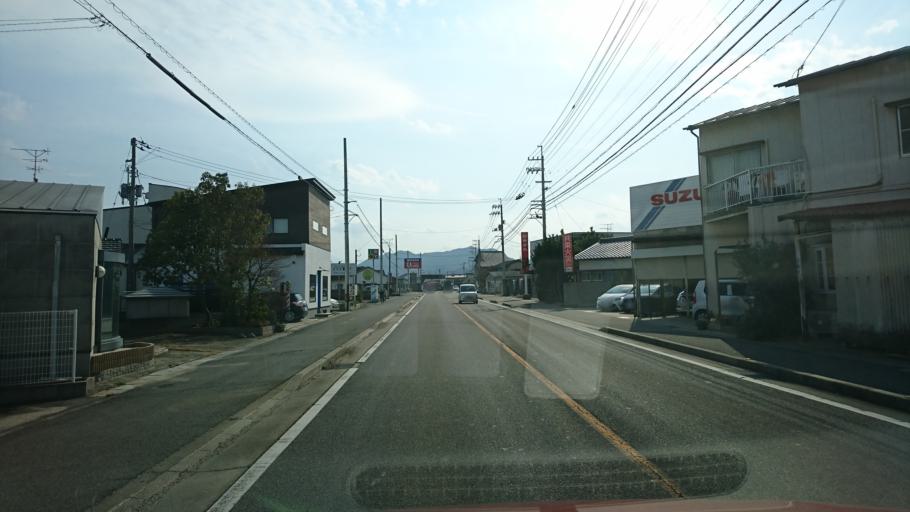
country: JP
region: Ehime
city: Saijo
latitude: 34.0246
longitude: 133.0381
